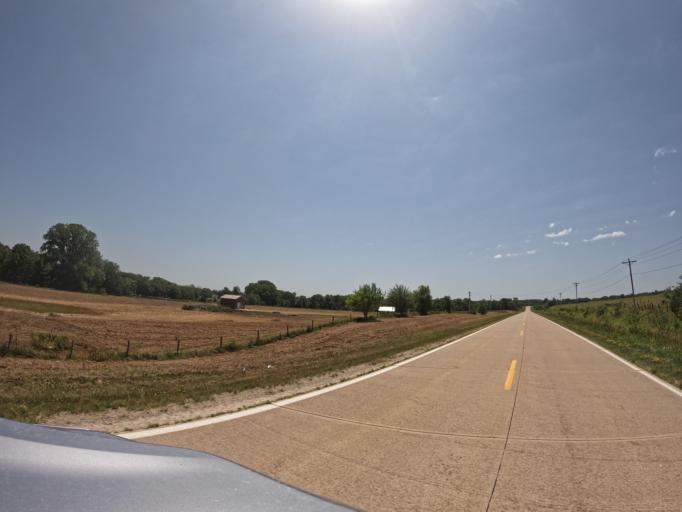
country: US
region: Iowa
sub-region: Henry County
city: Mount Pleasant
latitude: 40.9262
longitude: -91.5545
